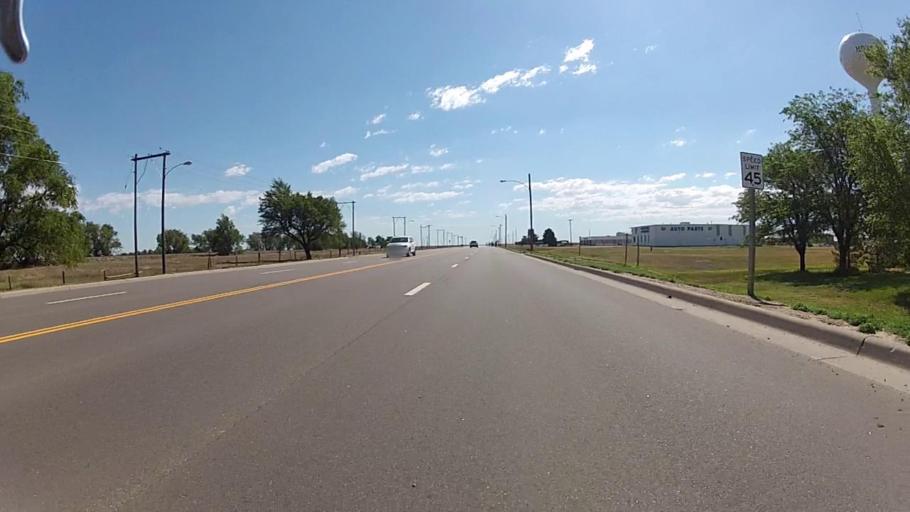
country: US
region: Kansas
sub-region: Gray County
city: Cimarron
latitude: 37.6003
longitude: -100.4380
